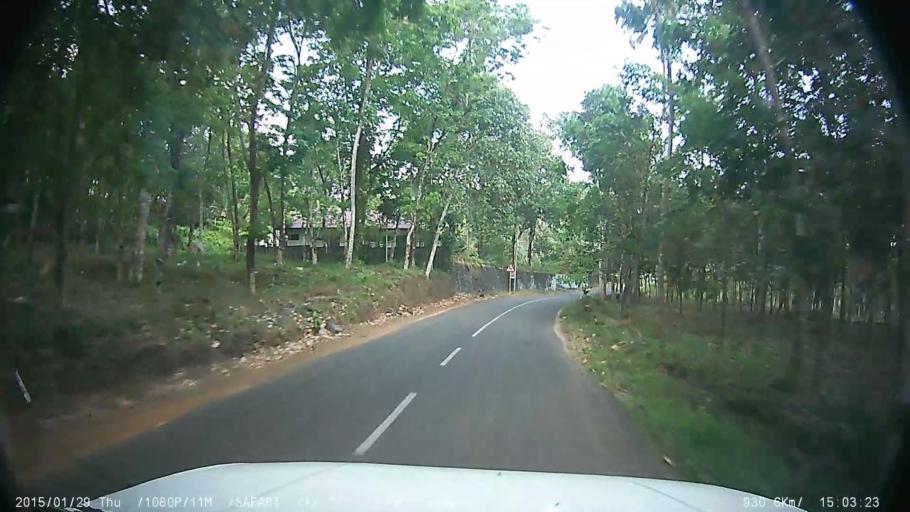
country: IN
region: Kerala
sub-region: Kottayam
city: Palackattumala
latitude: 9.7267
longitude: 76.5812
